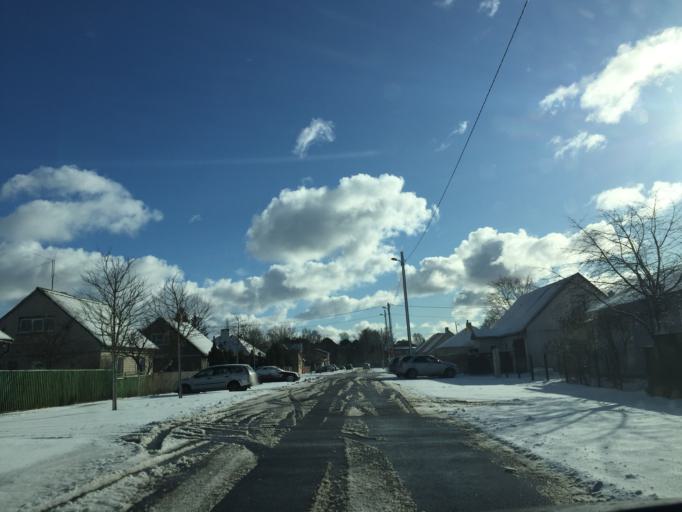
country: LV
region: Ventspils
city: Ventspils
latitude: 57.3812
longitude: 21.5553
